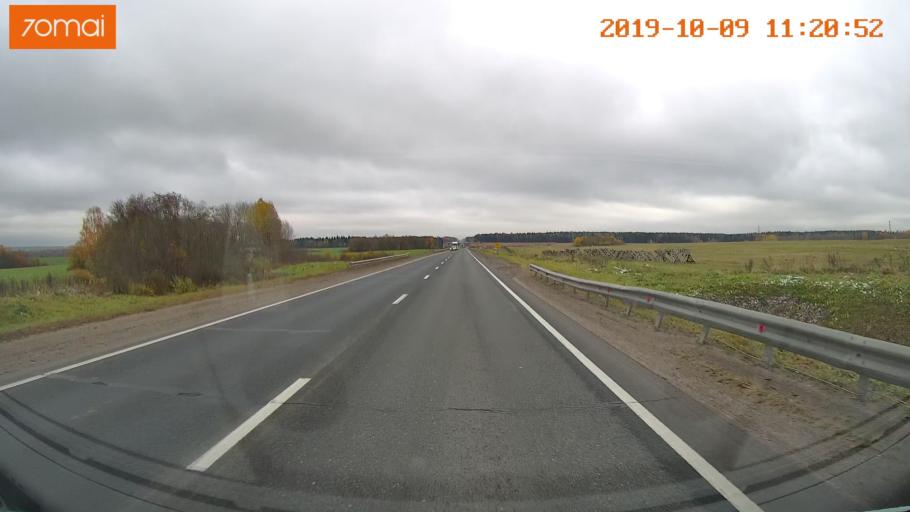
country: RU
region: Vologda
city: Vologda
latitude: 59.1448
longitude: 39.9437
